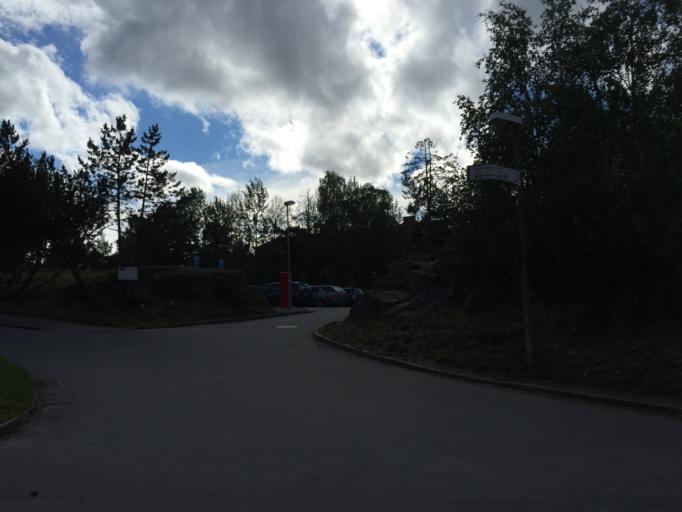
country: SE
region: Stockholm
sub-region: Stockholms Kommun
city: Arsta
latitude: 59.2963
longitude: 18.0522
